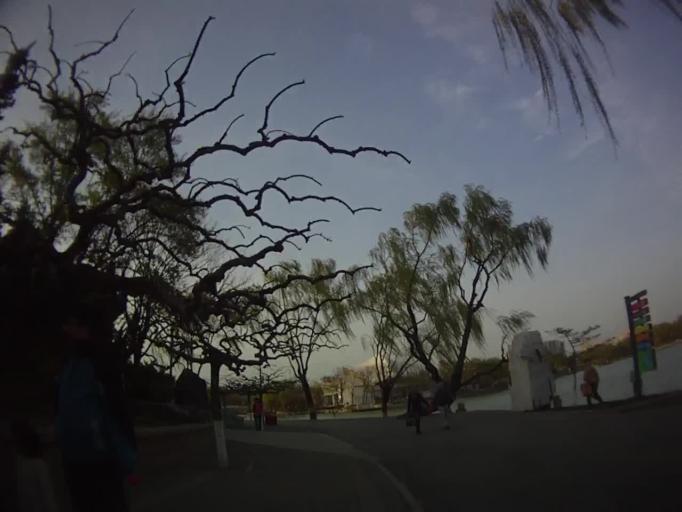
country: CN
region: Beijing
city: Longtan
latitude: 39.8763
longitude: 116.4326
